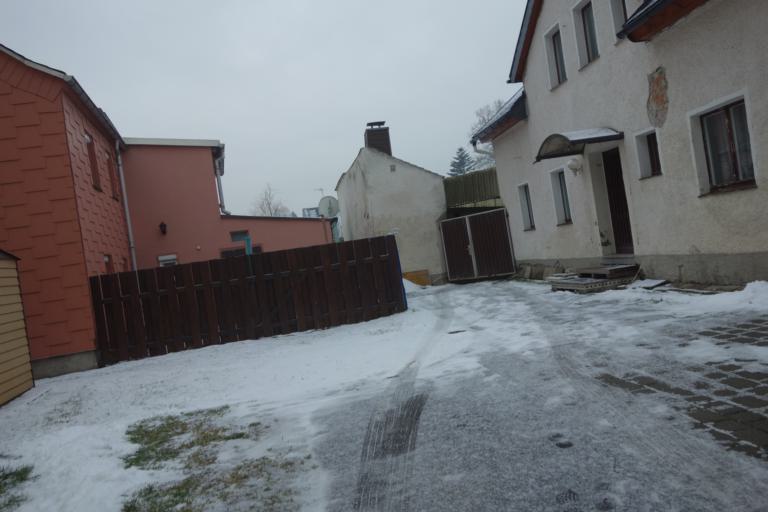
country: DE
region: Saxony
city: Freiberg
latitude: 50.9219
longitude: 13.3328
